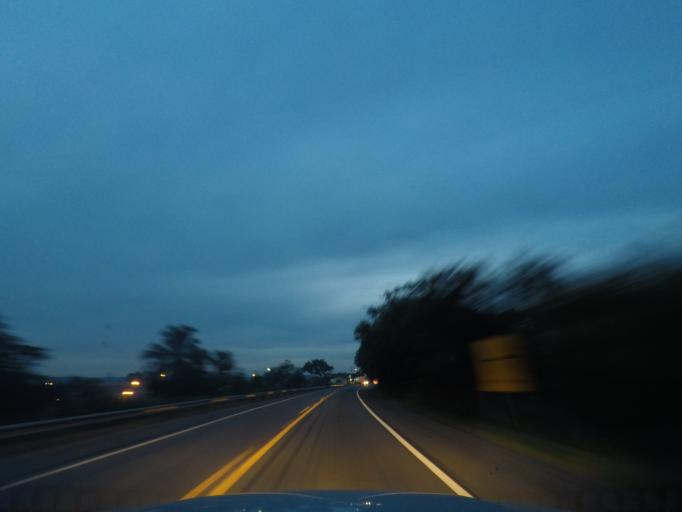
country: BR
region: Bahia
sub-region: Andarai
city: Vera Cruz
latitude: -12.5010
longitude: -41.2877
